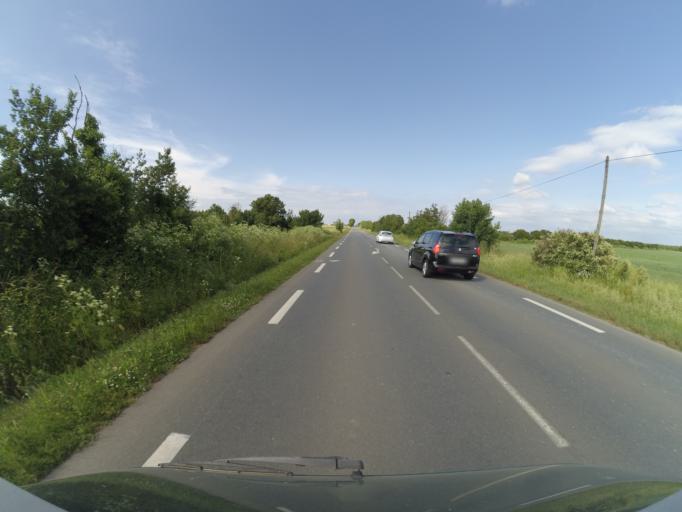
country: FR
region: Poitou-Charentes
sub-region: Departement de la Charente-Maritime
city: Saint-Xandre
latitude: 46.2287
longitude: -1.0799
